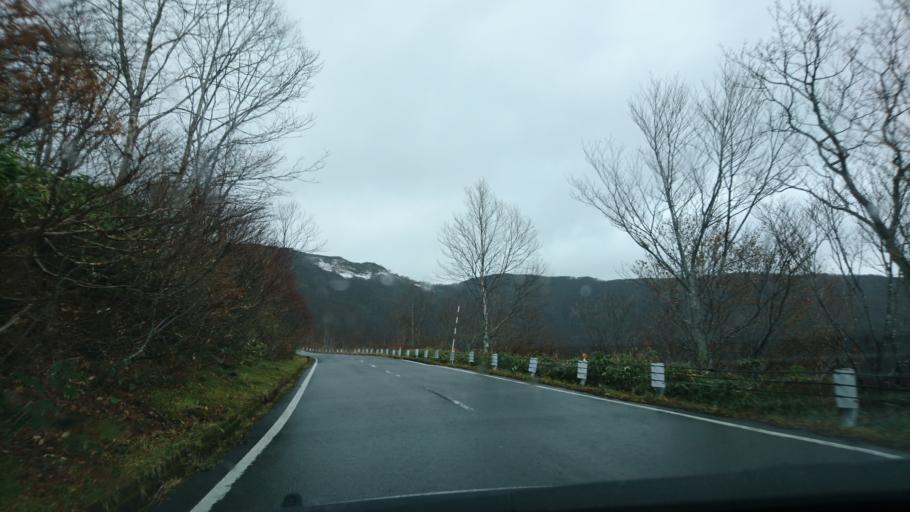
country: JP
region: Iwate
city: Ichinoseki
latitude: 38.9440
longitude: 140.8138
